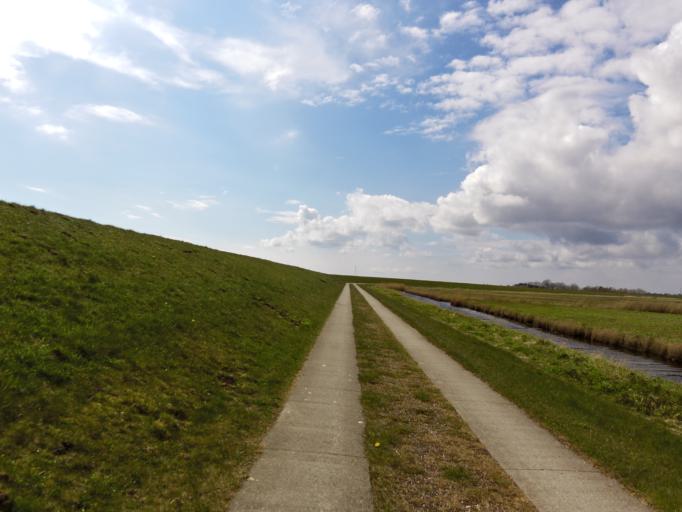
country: DE
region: Mecklenburg-Vorpommern
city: Barth
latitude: 54.4158
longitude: 12.7423
